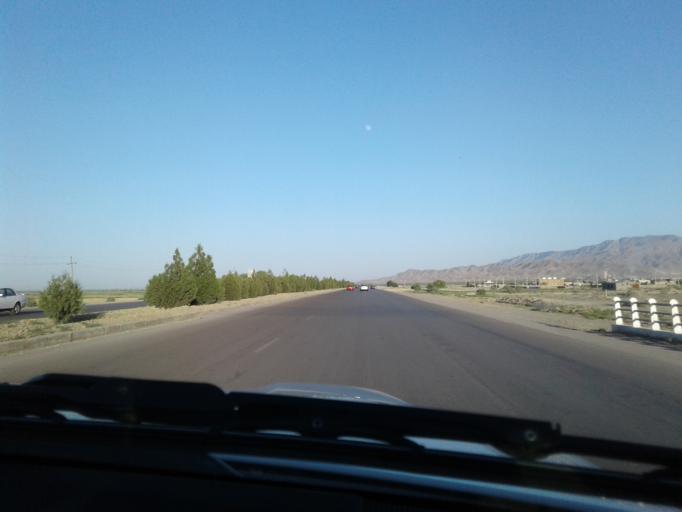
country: TM
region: Ahal
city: Baharly
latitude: 38.3079
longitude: 57.6183
